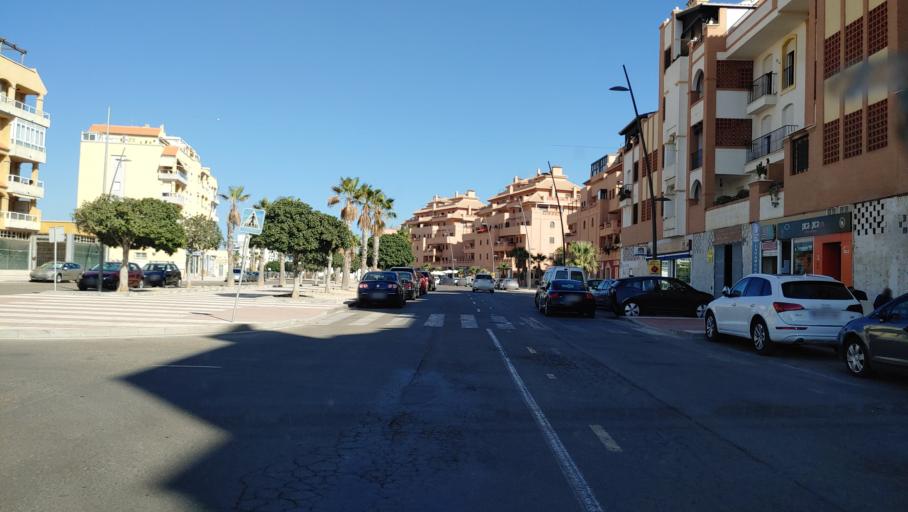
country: ES
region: Andalusia
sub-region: Provincia de Almeria
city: Roquetas de Mar
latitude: 36.7731
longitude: -2.6081
